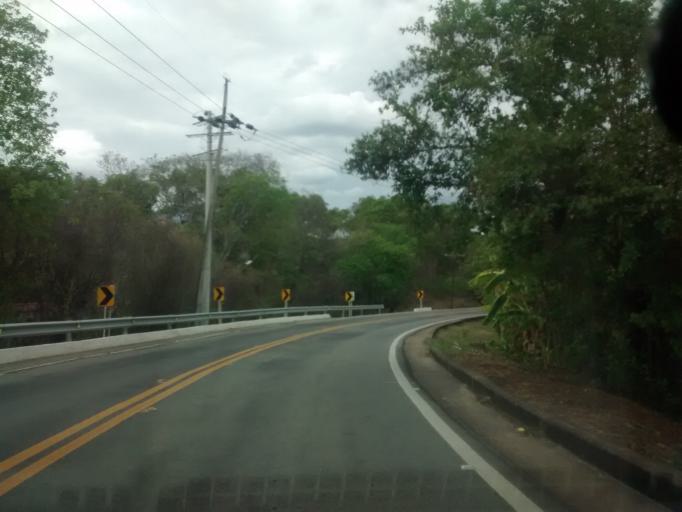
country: CO
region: Cundinamarca
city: Tocaima
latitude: 4.4428
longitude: -74.6730
